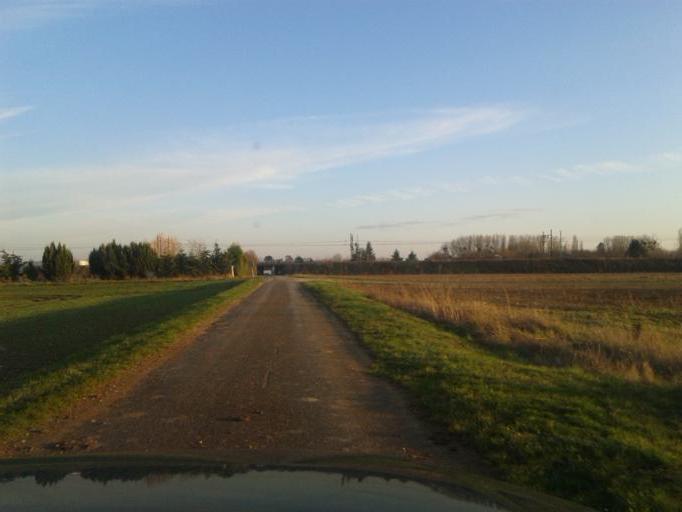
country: FR
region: Centre
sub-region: Departement du Loiret
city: Tavers
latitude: 47.7660
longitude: 1.6029
